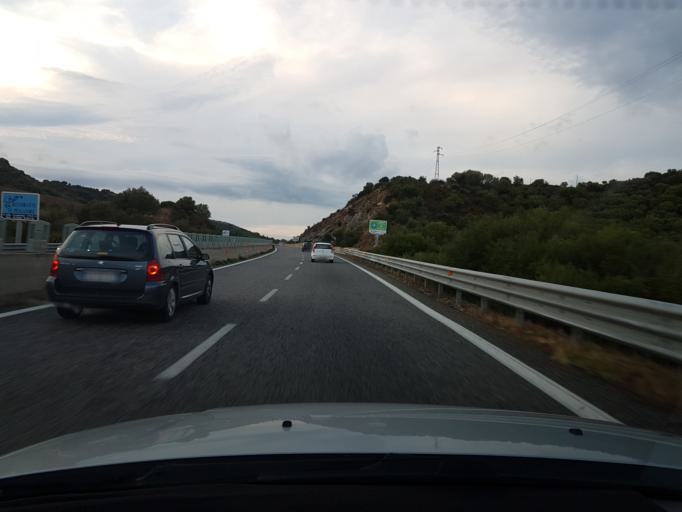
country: IT
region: Sardinia
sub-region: Provincia di Olbia-Tempio
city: San Teodoro
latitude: 40.7340
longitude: 9.6493
